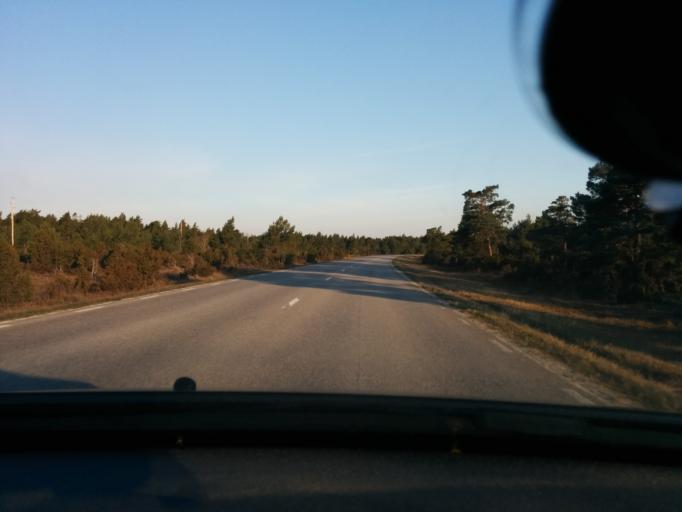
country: SE
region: Gotland
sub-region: Gotland
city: Visby
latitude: 57.6326
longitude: 18.4112
